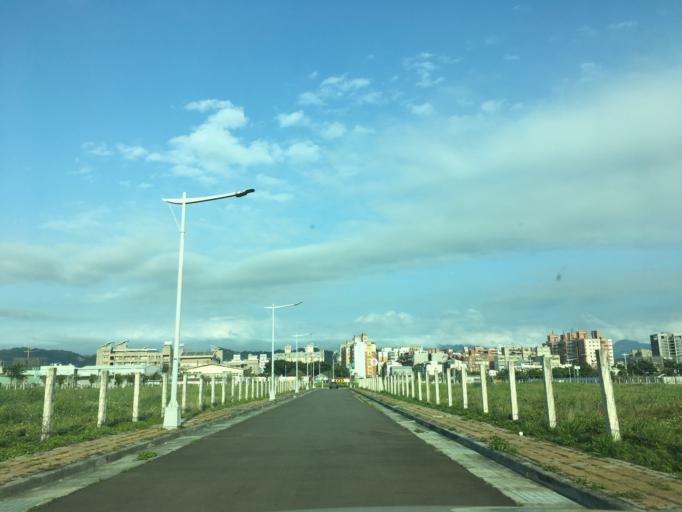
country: TW
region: Taiwan
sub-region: Taichung City
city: Taichung
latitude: 24.1960
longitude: 120.6909
